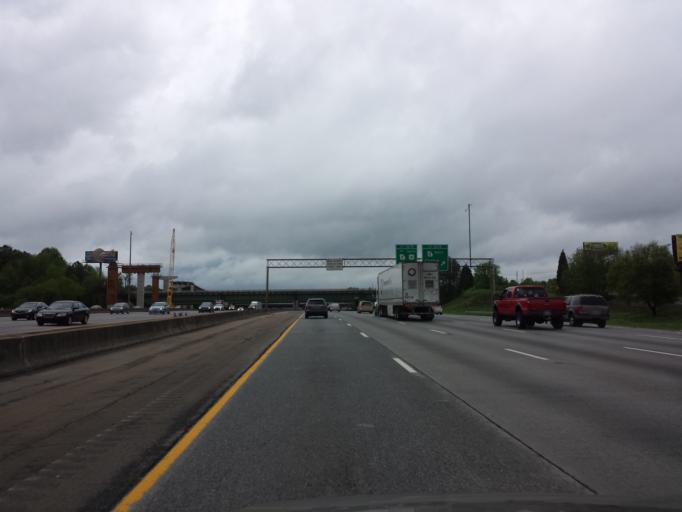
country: US
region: Georgia
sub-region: Cobb County
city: Marietta
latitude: 33.9795
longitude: -84.5370
